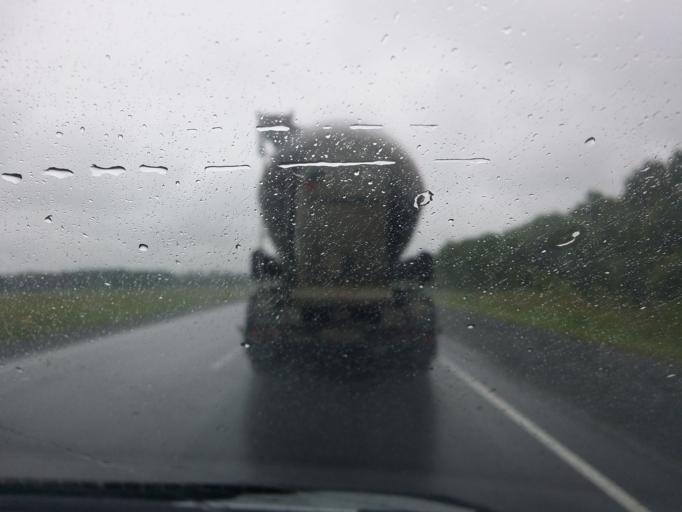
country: RU
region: Altai Krai
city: Bayunovskiye Klyuchi
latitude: 53.3040
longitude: 84.2593
